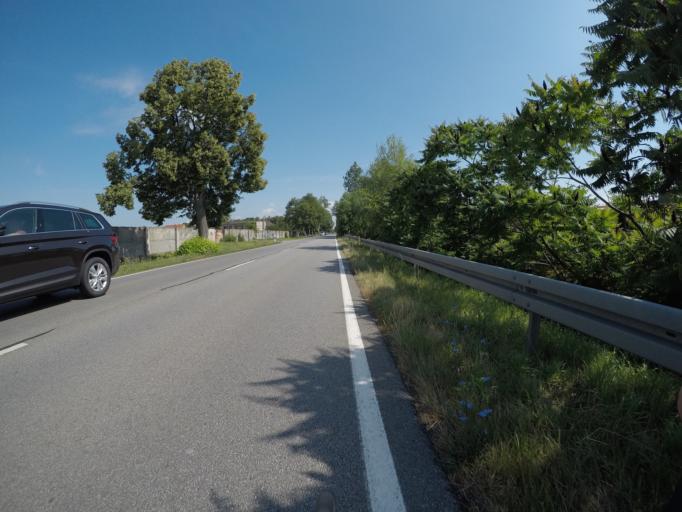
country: DE
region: Brandenburg
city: Bernau bei Berlin
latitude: 52.6617
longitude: 13.5771
